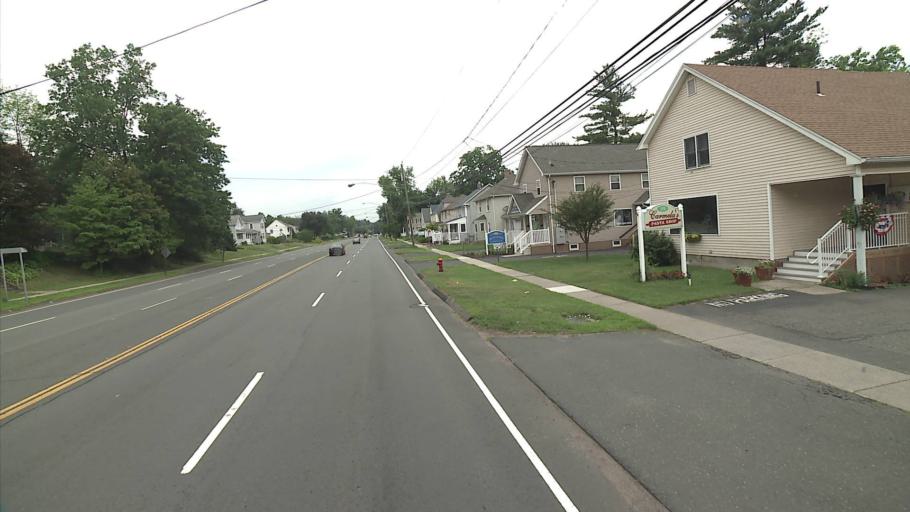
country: US
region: Connecticut
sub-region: Hartford County
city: Wethersfield
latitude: 41.7173
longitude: -72.6657
